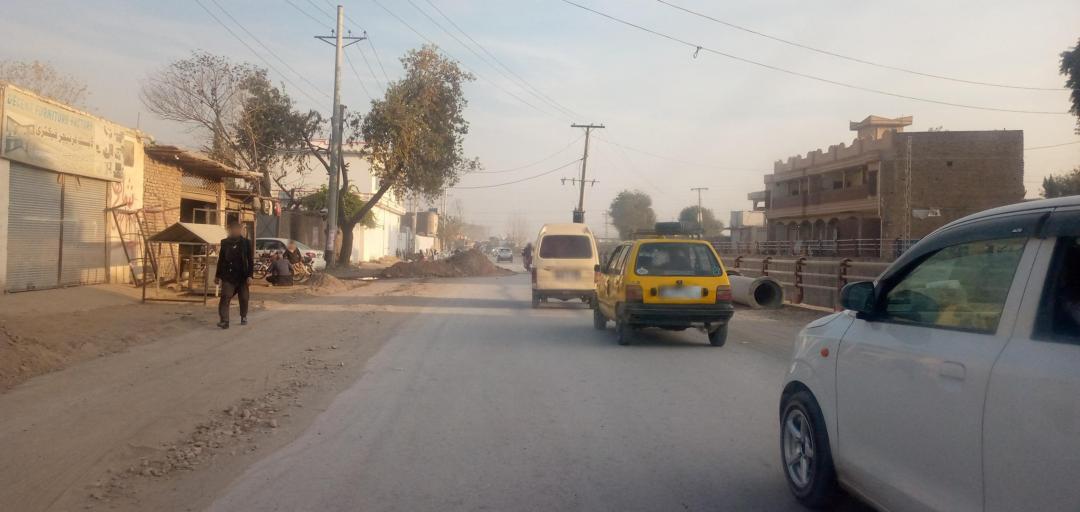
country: PK
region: Khyber Pakhtunkhwa
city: Peshawar
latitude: 33.9700
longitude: 71.5359
